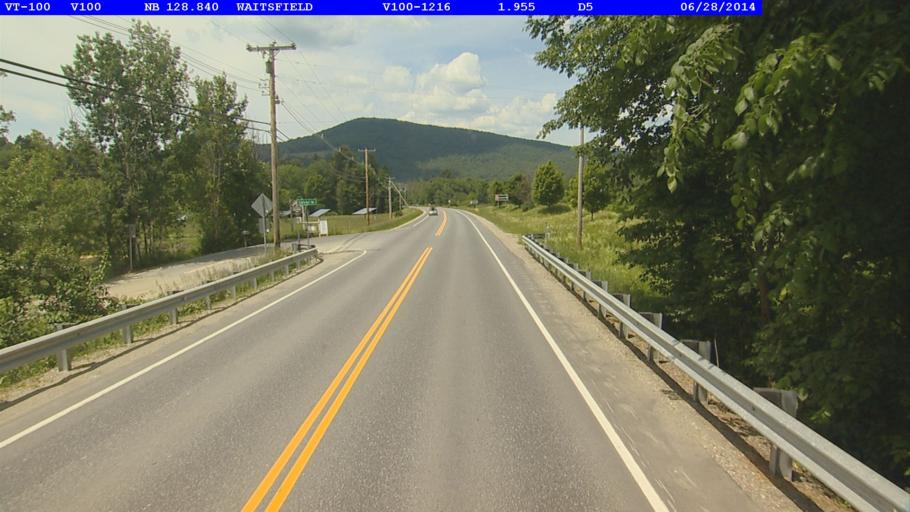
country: US
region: Vermont
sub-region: Washington County
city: Northfield
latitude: 44.1735
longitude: -72.8329
